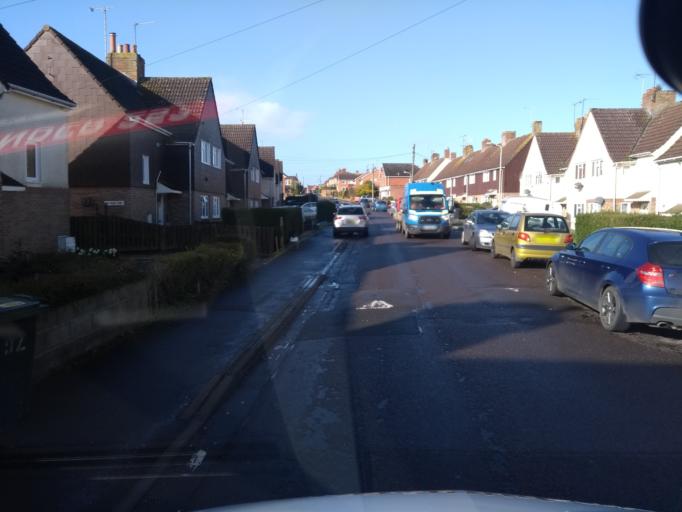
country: GB
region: England
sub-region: Somerset
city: Yeovil
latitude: 50.9499
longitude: -2.6153
